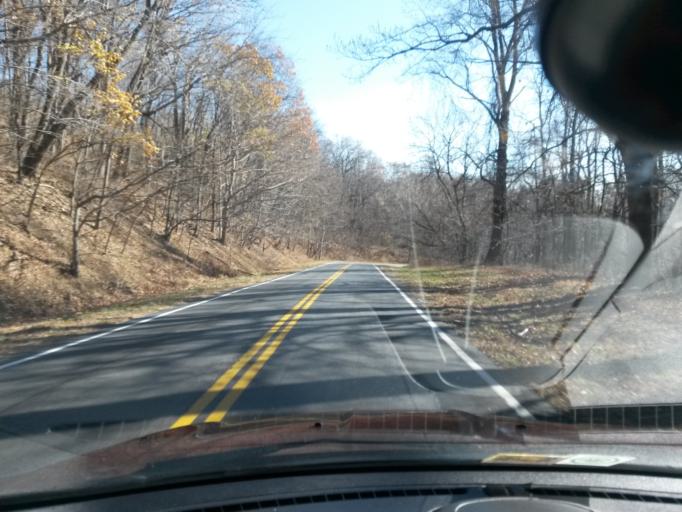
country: US
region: Virginia
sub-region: City of Bedford
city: Bedford
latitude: 37.4398
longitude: -79.5870
